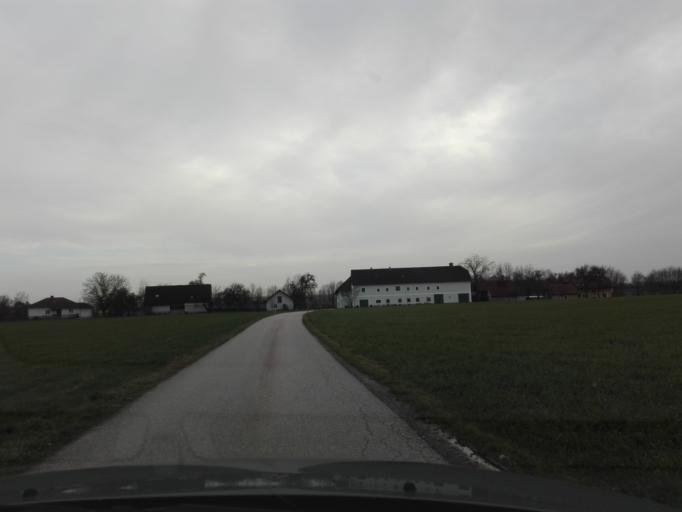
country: AT
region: Upper Austria
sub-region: Politischer Bezirk Linz-Land
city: Horsching
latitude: 48.2237
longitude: 14.1442
